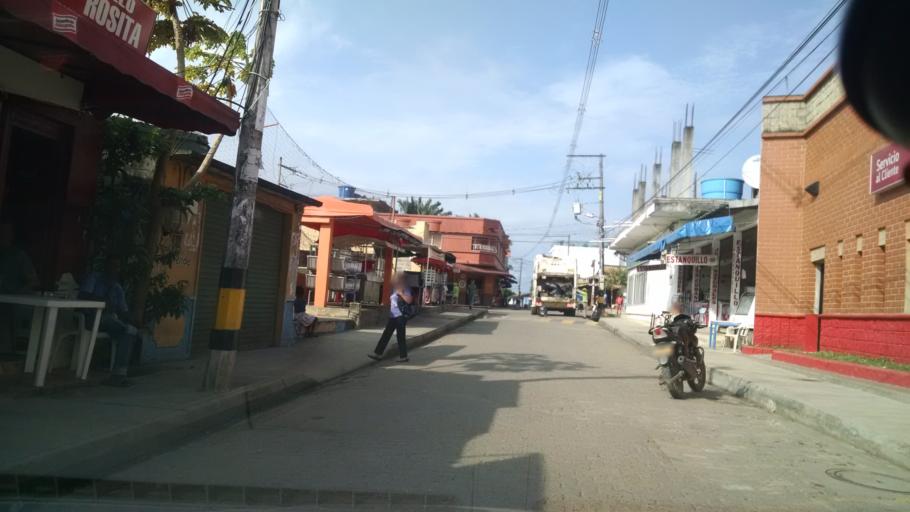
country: CO
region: Antioquia
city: Necocli
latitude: 8.4239
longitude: -76.7863
